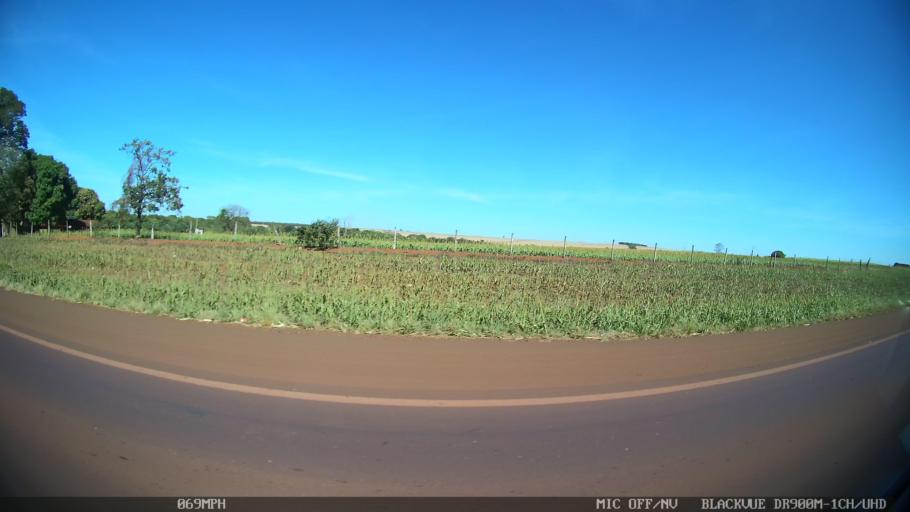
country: BR
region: Sao Paulo
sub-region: Ipua
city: Ipua
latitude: -20.4922
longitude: -47.9901
